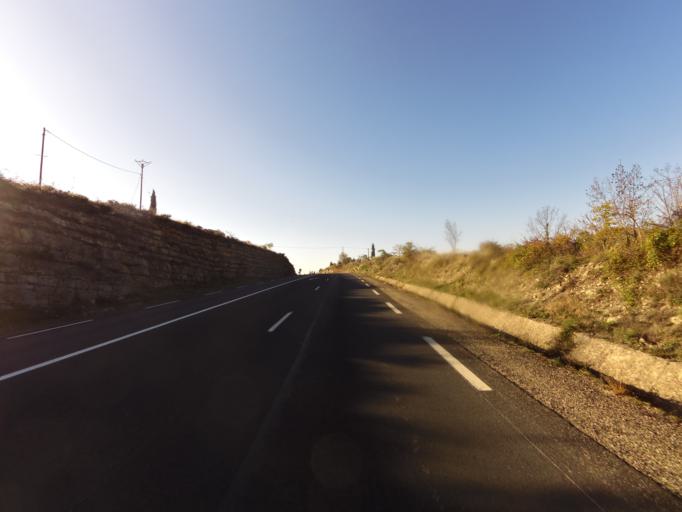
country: FR
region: Rhone-Alpes
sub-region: Departement de l'Ardeche
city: Lablachere
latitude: 44.4651
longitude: 4.2278
